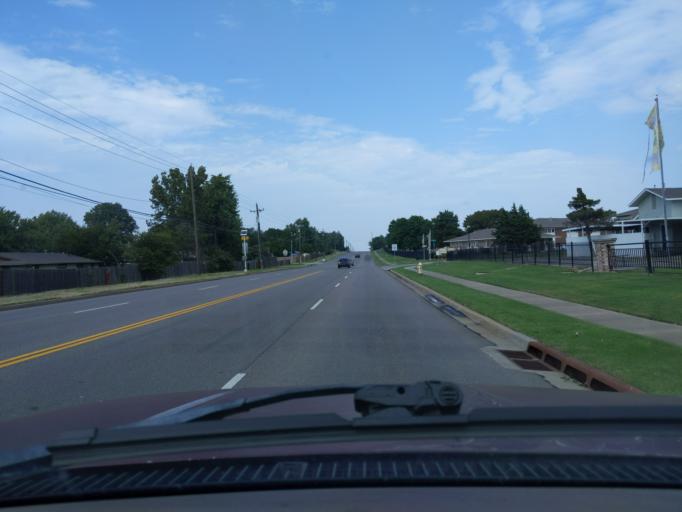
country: US
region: Oklahoma
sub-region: Tulsa County
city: Broken Arrow
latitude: 36.1376
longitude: -95.8332
